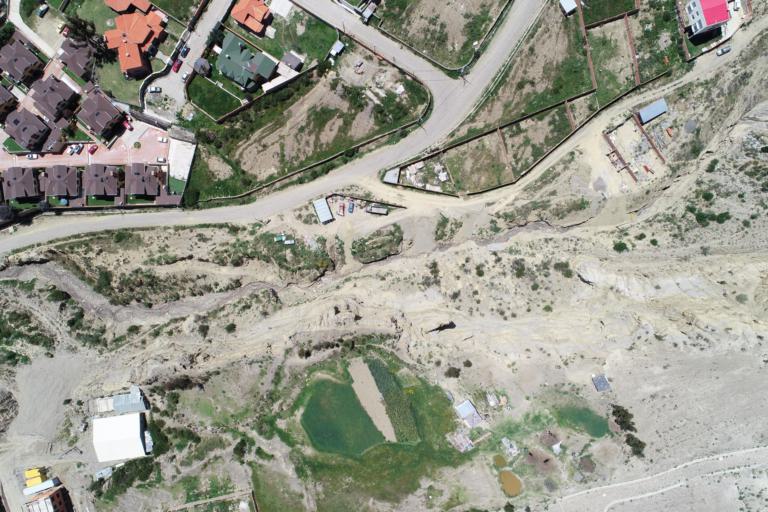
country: BO
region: La Paz
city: La Paz
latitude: -16.5198
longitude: -68.0535
